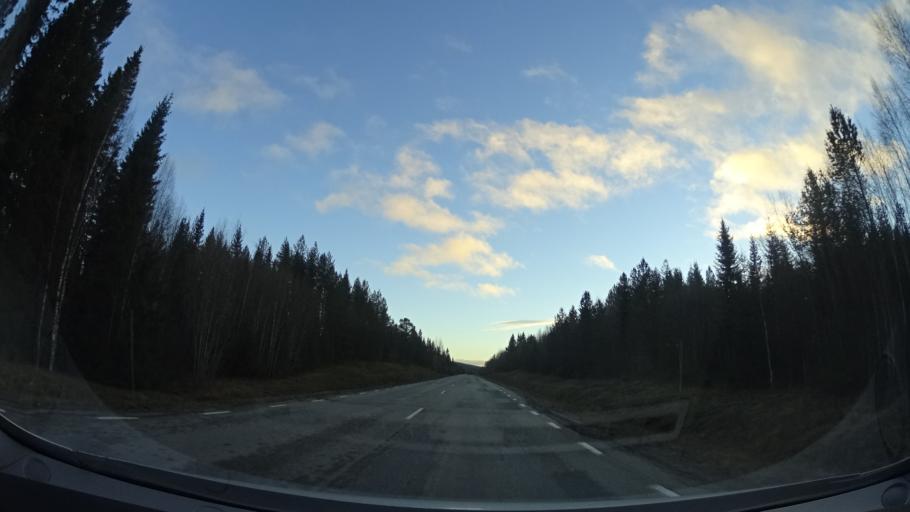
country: SE
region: Jaemtland
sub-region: Stroemsunds Kommun
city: Stroemsund
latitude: 64.0456
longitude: 15.5415
